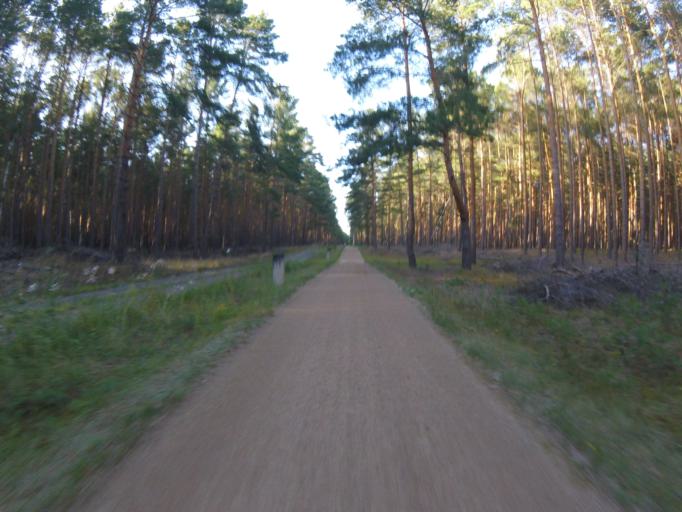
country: DE
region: Brandenburg
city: Munchehofe
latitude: 52.1991
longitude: 13.7655
